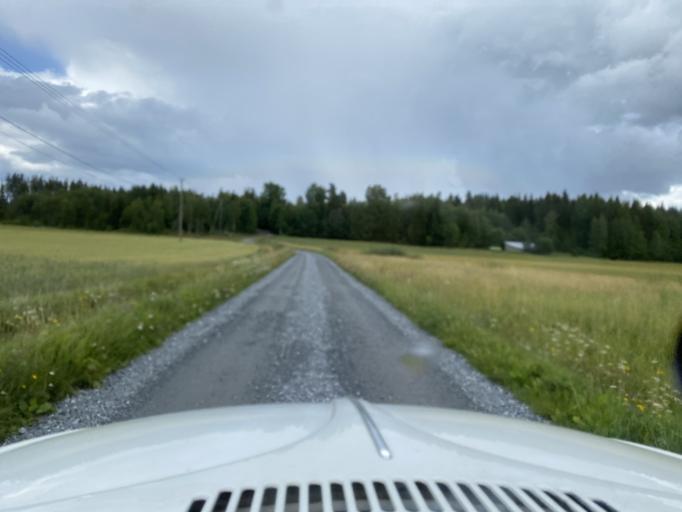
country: FI
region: Pirkanmaa
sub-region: Lounais-Pirkanmaa
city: Punkalaidun
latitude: 61.1254
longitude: 23.0627
